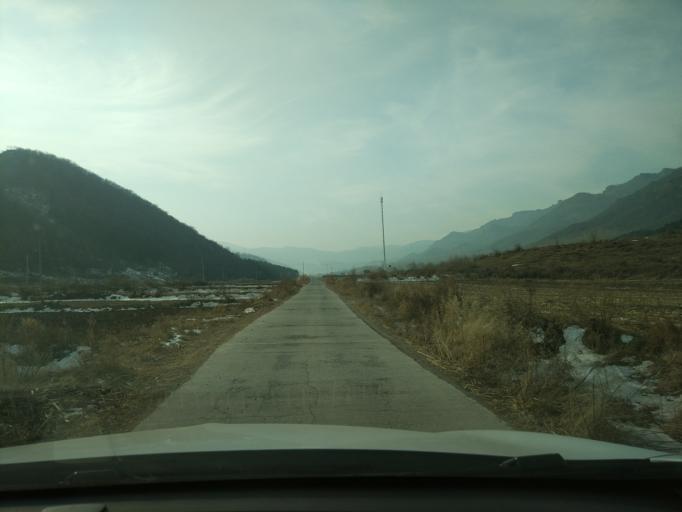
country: CN
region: Hebei
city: Xiwanzi
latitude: 40.8248
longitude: 115.5034
